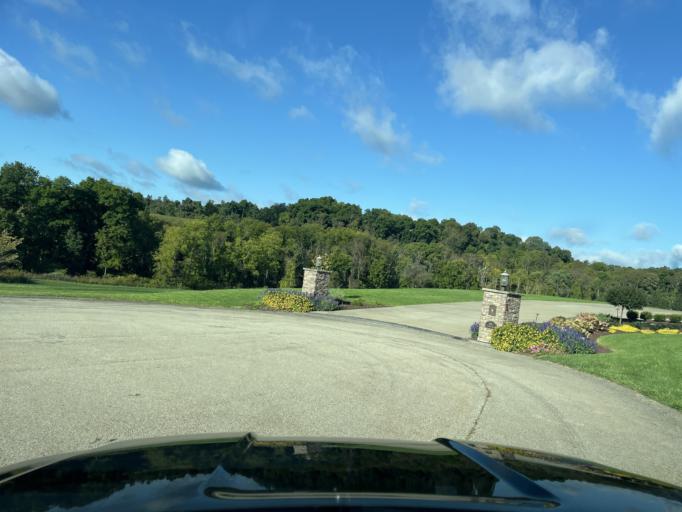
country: US
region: Pennsylvania
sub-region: Fayette County
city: South Uniontown
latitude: 39.8844
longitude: -79.7557
